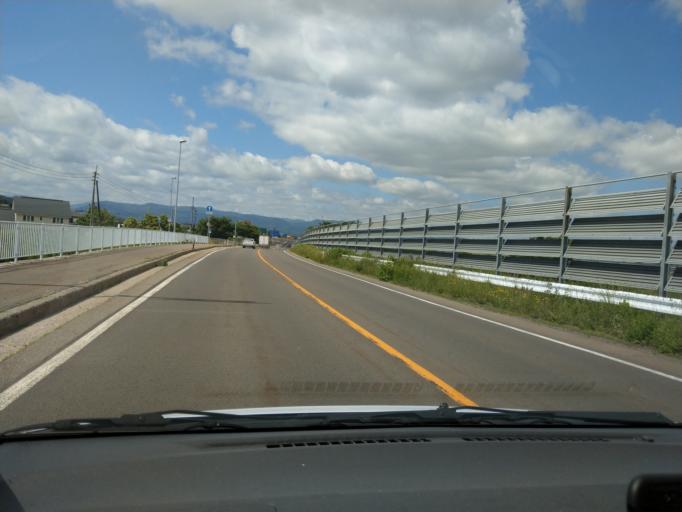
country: JP
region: Akita
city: Yuzawa
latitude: 39.2082
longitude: 140.5096
